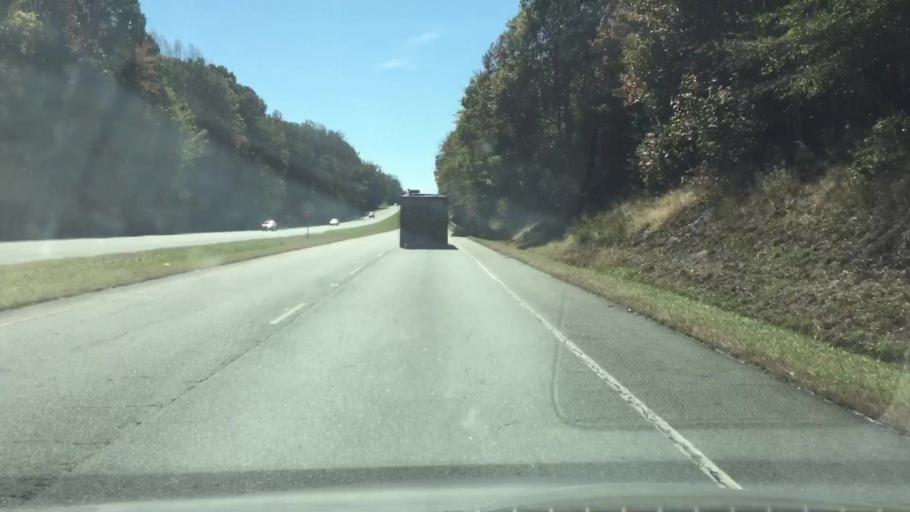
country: US
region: North Carolina
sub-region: Rockingham County
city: Reidsville
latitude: 36.2386
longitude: -79.6714
